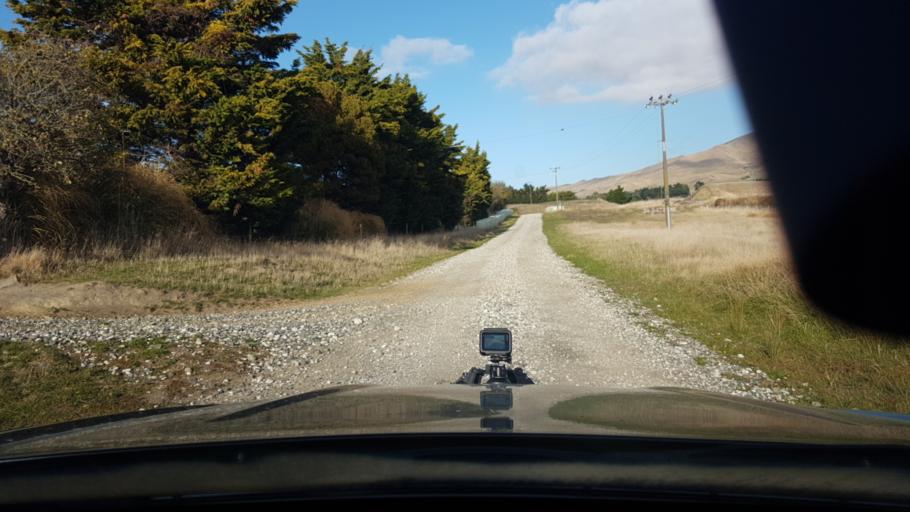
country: NZ
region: Marlborough
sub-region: Marlborough District
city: Blenheim
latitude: -41.8369
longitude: 174.1264
